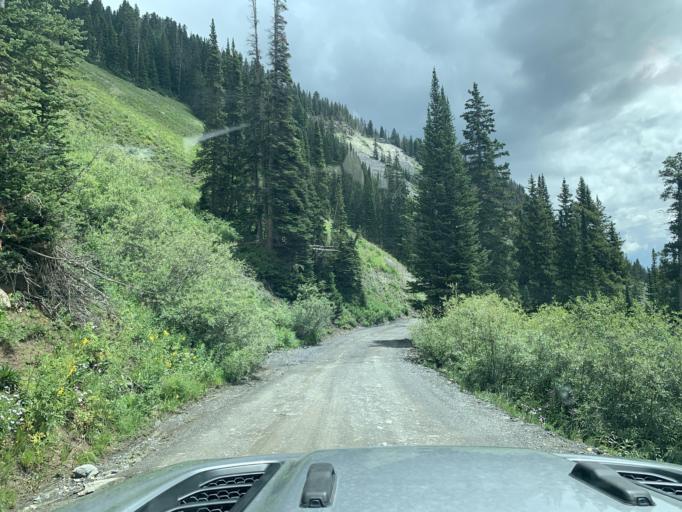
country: US
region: Colorado
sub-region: Gunnison County
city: Crested Butte
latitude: 39.0139
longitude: -107.0443
